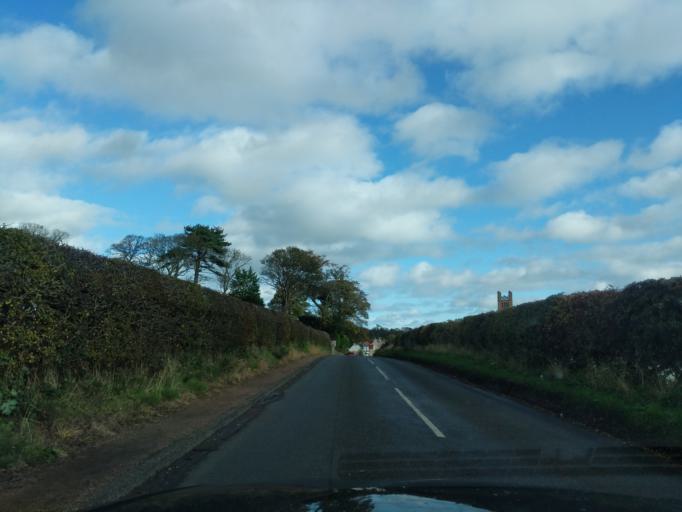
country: GB
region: Scotland
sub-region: Fife
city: Saint Monance
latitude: 56.2073
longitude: -2.8353
